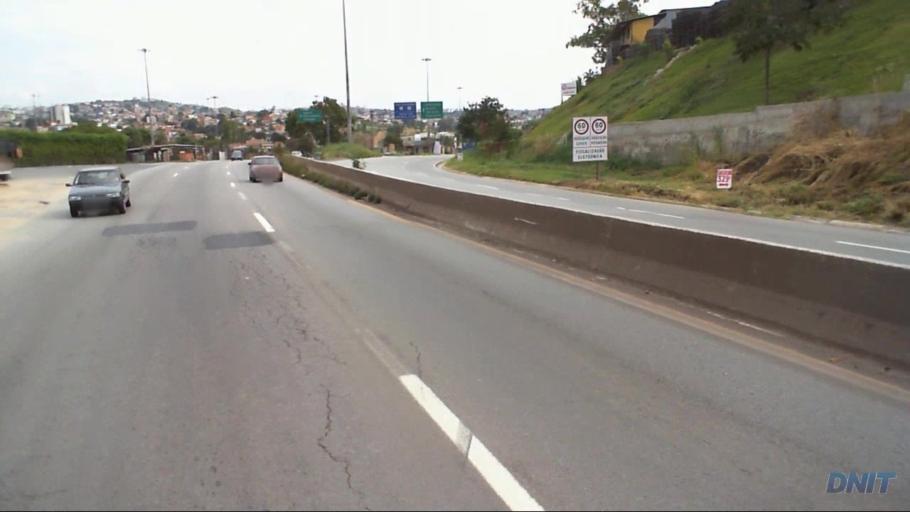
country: BR
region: Minas Gerais
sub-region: Belo Horizonte
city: Belo Horizonte
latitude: -19.8543
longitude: -43.8908
